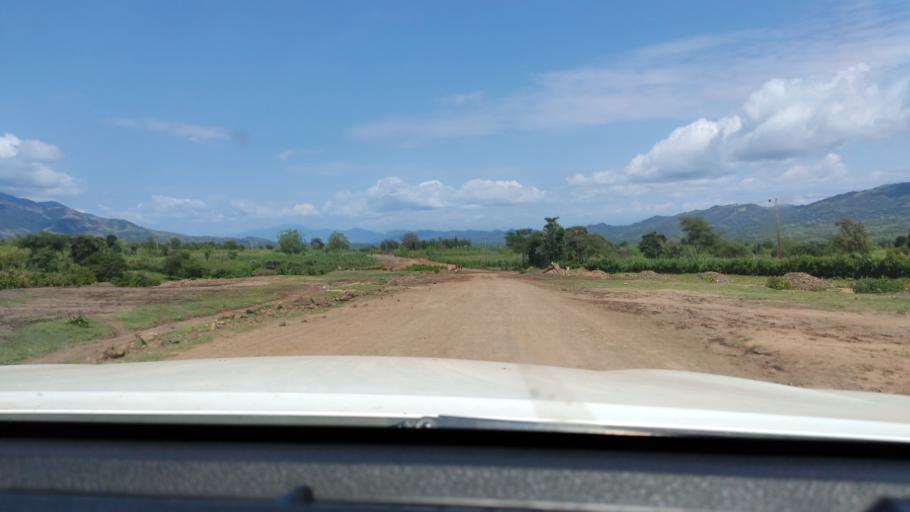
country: ET
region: Southern Nations, Nationalities, and People's Region
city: Felege Neway
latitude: 6.3652
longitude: 36.9901
